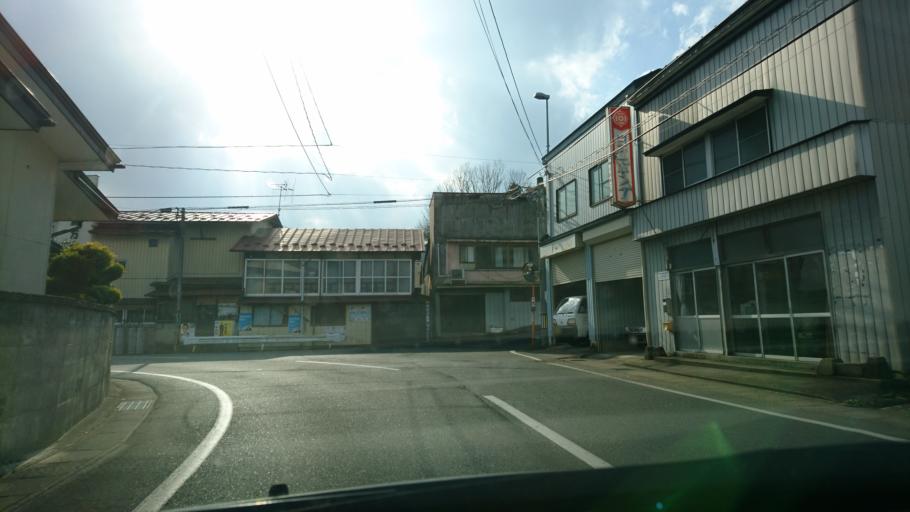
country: JP
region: Iwate
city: Mizusawa
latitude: 39.0448
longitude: 141.1212
